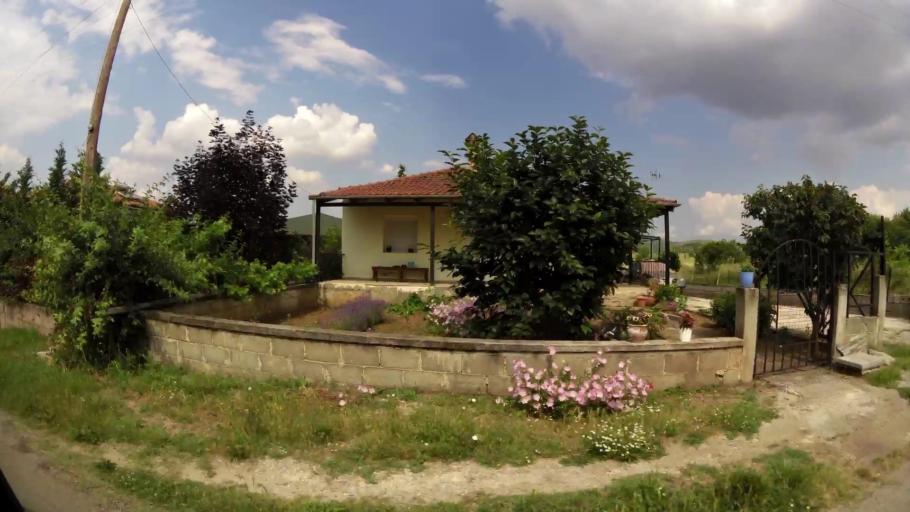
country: GR
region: West Macedonia
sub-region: Nomos Kozanis
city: Koila
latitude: 40.3522
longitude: 21.8380
